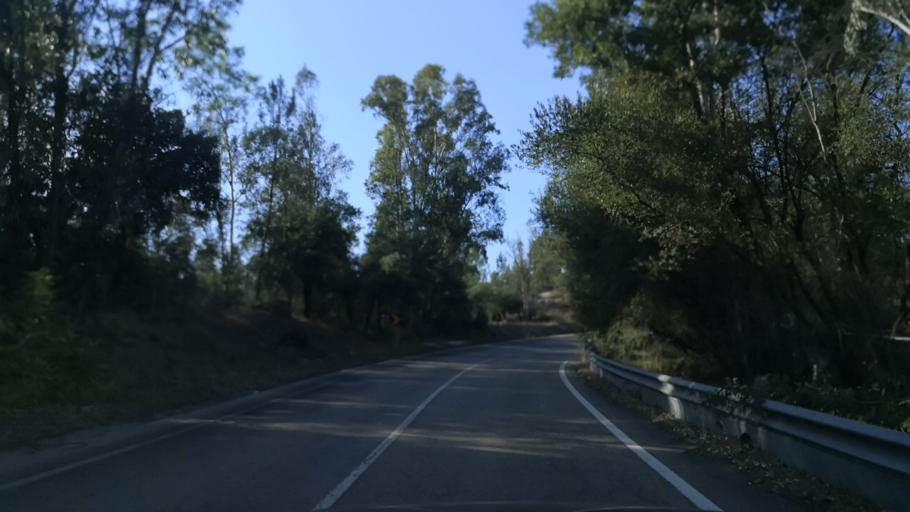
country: PT
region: Santarem
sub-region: Almeirim
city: Fazendas de Almeirim
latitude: 39.0676
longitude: -8.5656
